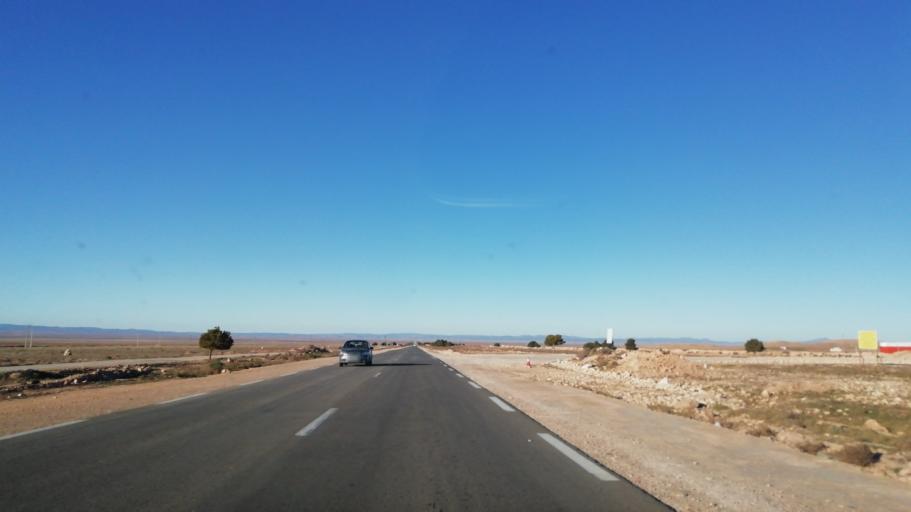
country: DZ
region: Tlemcen
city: Sebdou
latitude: 34.3003
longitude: -1.2611
